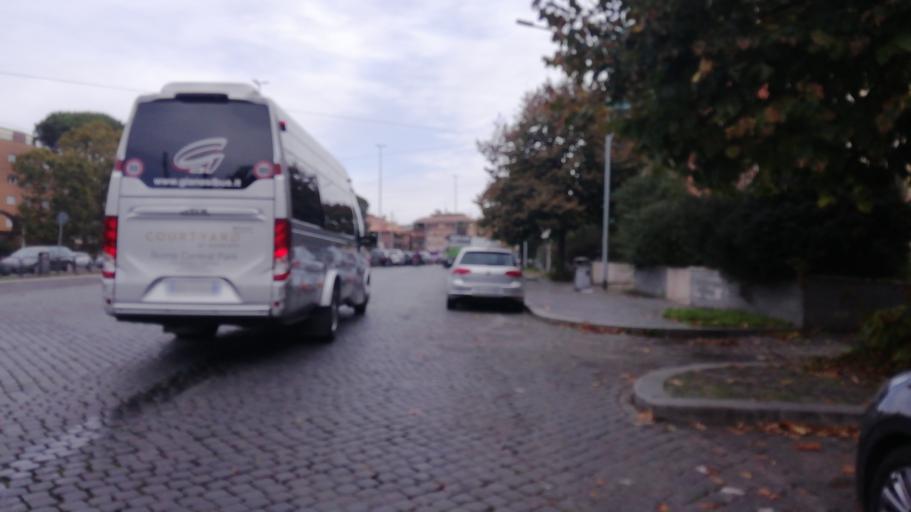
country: IT
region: Latium
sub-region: Citta metropolitana di Roma Capitale
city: Rome
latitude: 41.8790
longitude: 12.4831
